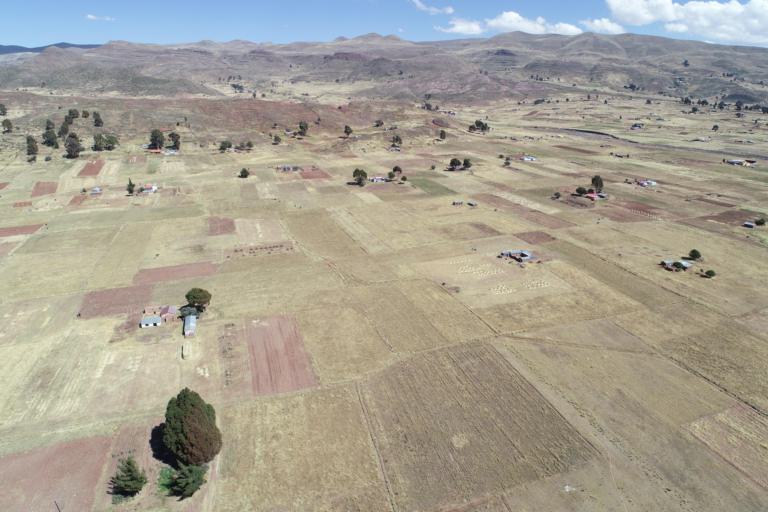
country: BO
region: La Paz
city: Tiahuanaco
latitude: -16.5955
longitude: -68.7768
